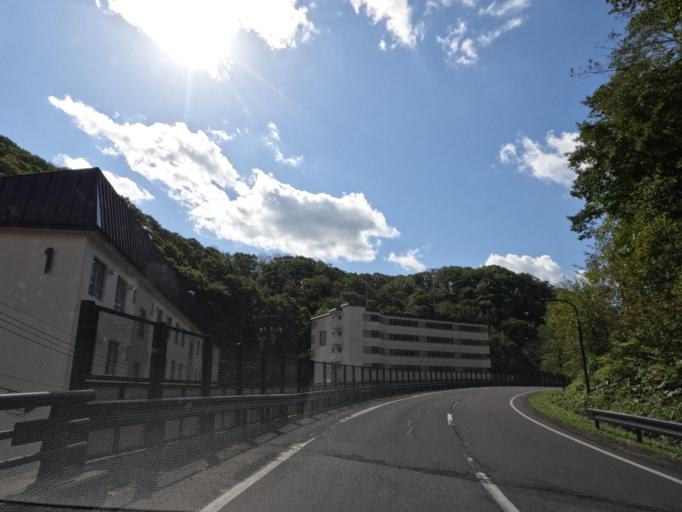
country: JP
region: Hokkaido
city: Shiraoi
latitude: 42.4873
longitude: 141.1479
